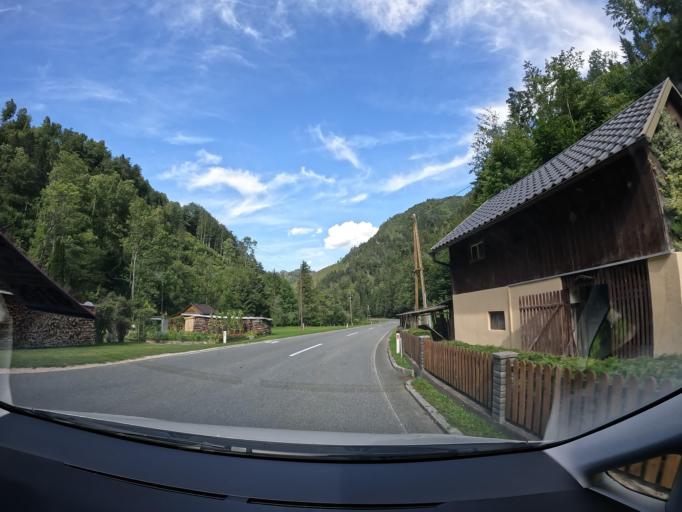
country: AT
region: Carinthia
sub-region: Politischer Bezirk Volkermarkt
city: Bad Eisenkappel
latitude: 46.4536
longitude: 14.5821
